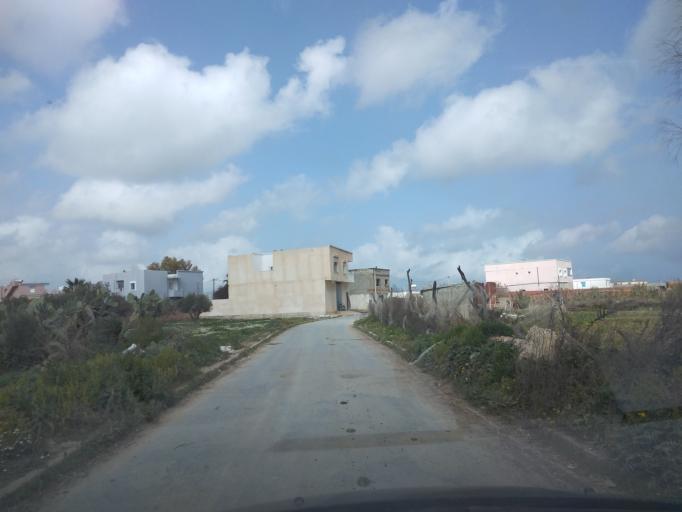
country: TN
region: Ariana
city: Qal'at al Andalus
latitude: 37.0665
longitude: 10.1257
